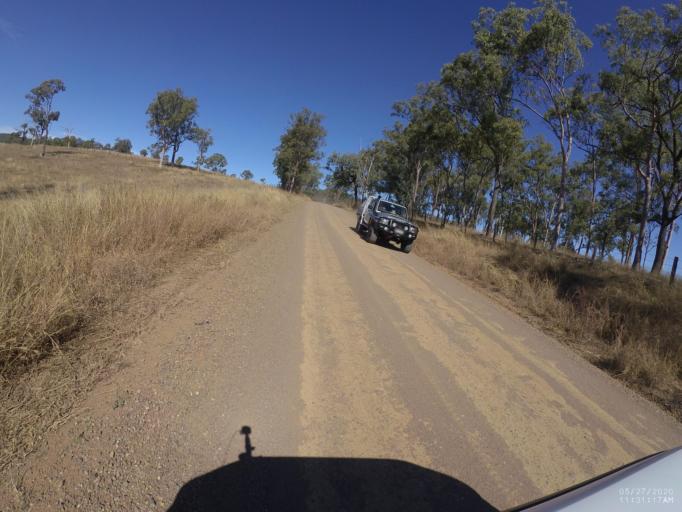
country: AU
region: Queensland
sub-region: Ipswich
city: Redbank Plains
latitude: -27.7420
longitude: 152.8309
